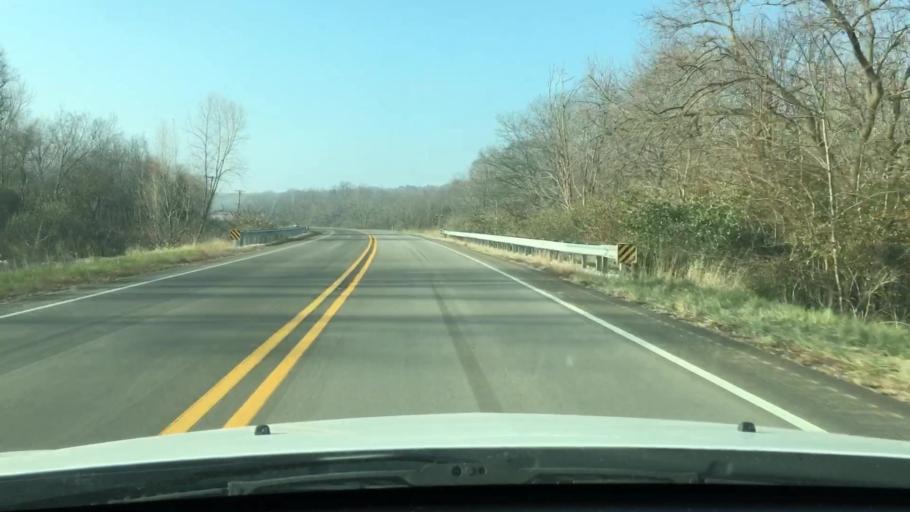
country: US
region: Illinois
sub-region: Peoria County
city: Glasford
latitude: 40.5490
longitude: -89.8533
